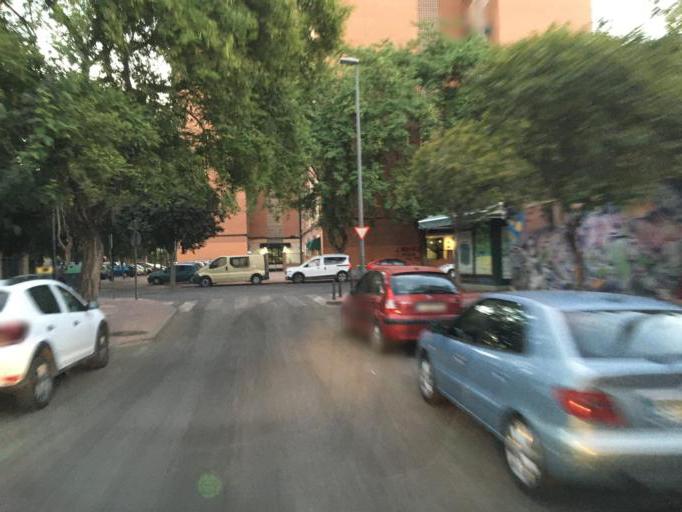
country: ES
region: Murcia
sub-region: Murcia
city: Murcia
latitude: 37.9880
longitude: -1.1223
